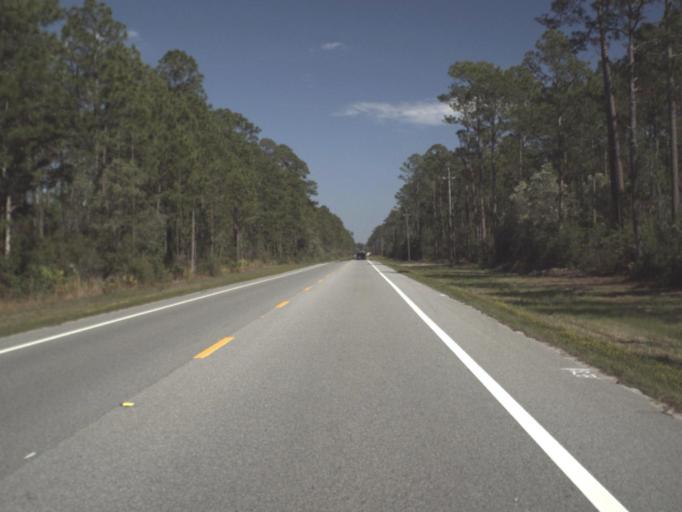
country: US
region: Florida
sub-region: Bay County
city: Lynn Haven
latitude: 30.3221
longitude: -85.6767
